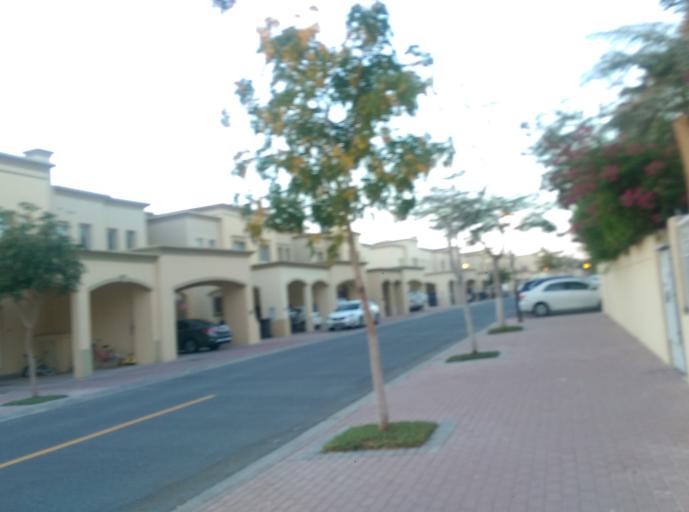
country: AE
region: Dubai
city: Dubai
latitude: 25.0507
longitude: 55.1743
